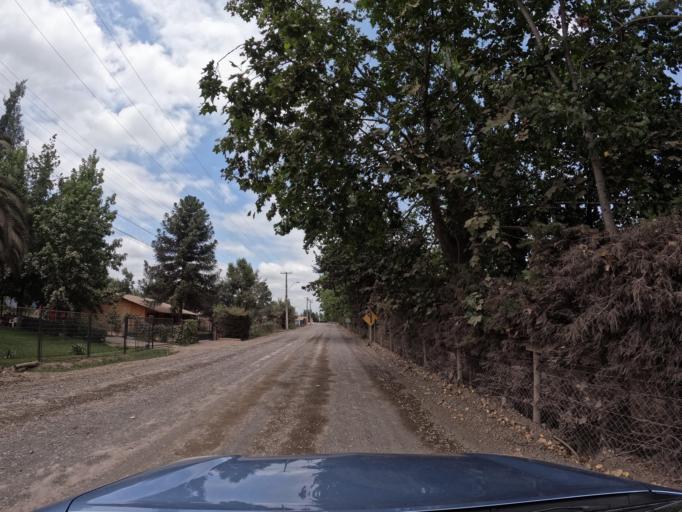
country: CL
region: O'Higgins
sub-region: Provincia de Colchagua
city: Chimbarongo
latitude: -34.7393
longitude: -70.9774
